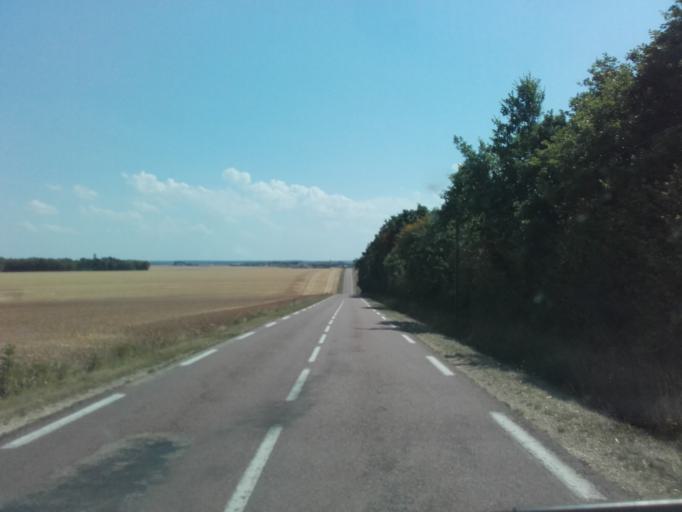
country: FR
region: Bourgogne
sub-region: Departement de l'Yonne
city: Joux-la-Ville
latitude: 47.6935
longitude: 3.8638
